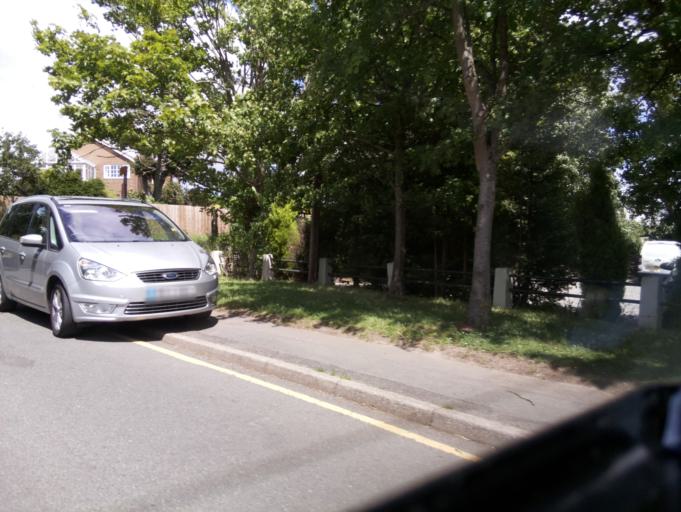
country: GB
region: England
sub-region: Nottinghamshire
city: Burton Joyce
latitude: 53.0010
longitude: -1.0663
